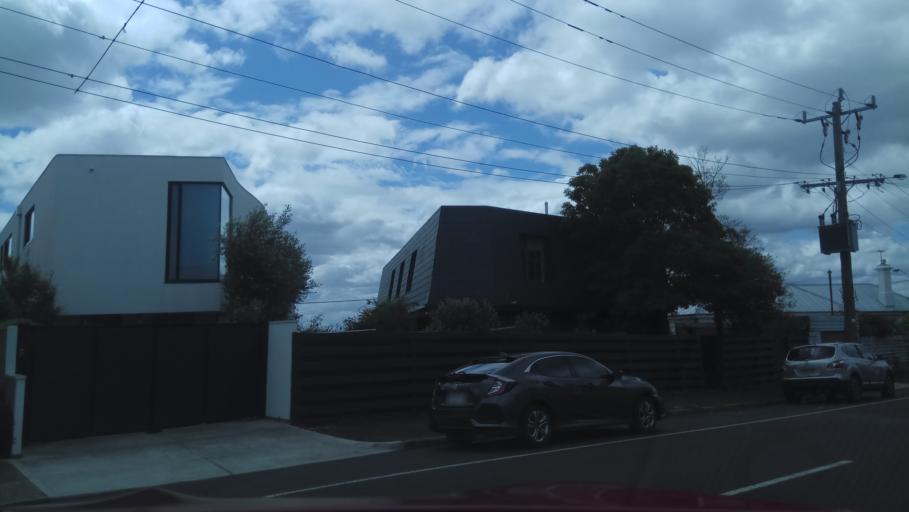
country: AU
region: Victoria
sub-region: Hobsons Bay
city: Williamstown
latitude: -37.8513
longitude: 144.8967
